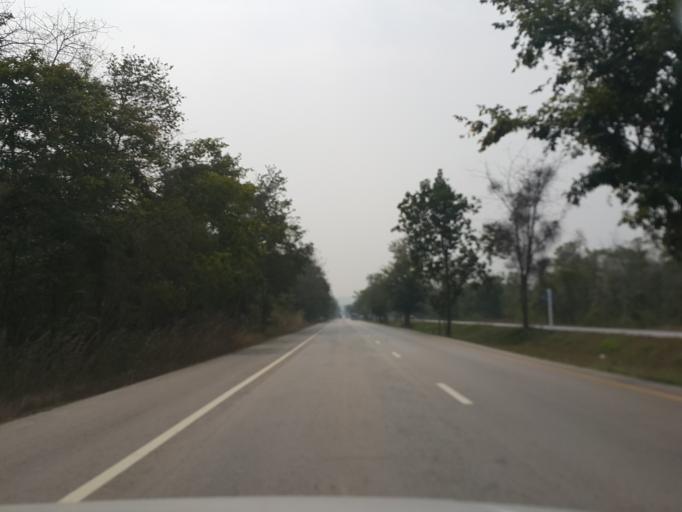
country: TH
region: Lampang
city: Ko Kha
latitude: 18.0855
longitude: 99.3953
